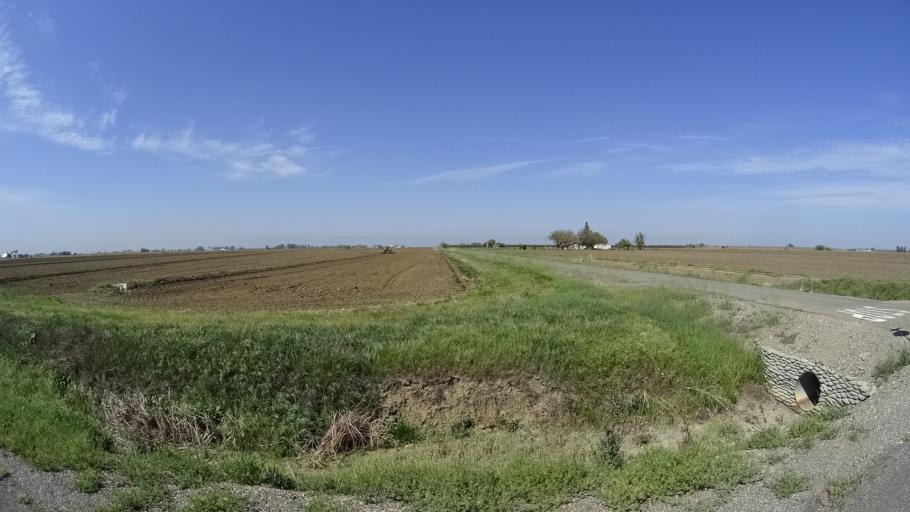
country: US
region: California
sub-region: Glenn County
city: Hamilton City
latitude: 39.6081
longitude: -122.0271
